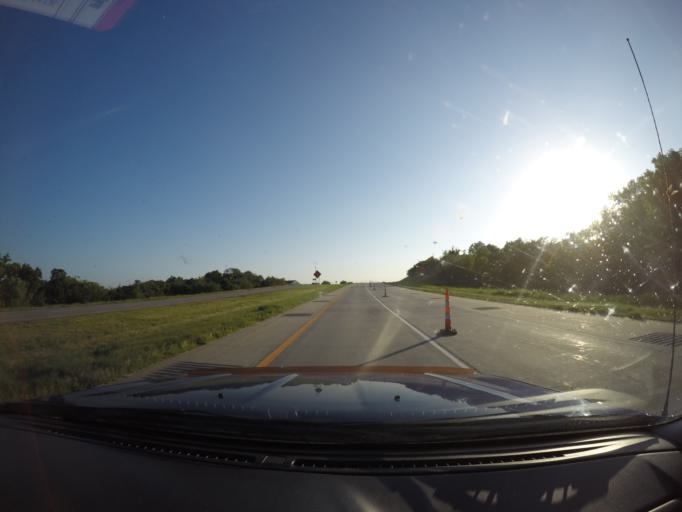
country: US
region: Kansas
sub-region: Pottawatomie County
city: Wamego
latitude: 39.2022
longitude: -96.4350
